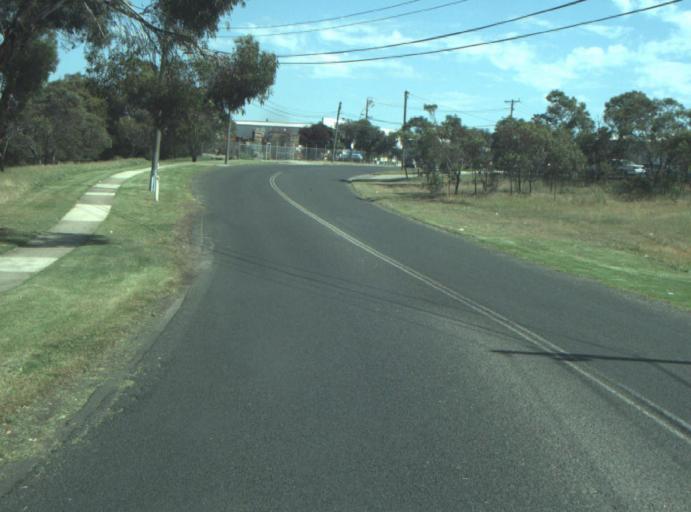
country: AU
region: Victoria
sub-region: Greater Geelong
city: Geelong West
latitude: -38.1266
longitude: 144.3508
